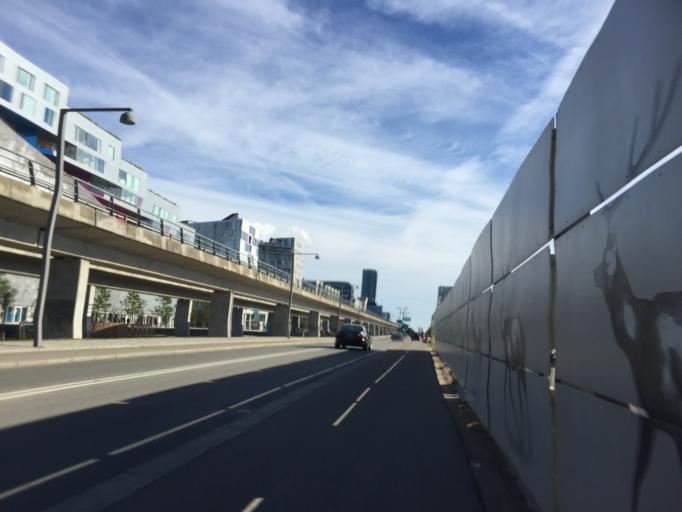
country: DK
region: Capital Region
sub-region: Tarnby Kommune
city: Tarnby
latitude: 55.6361
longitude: 12.5818
